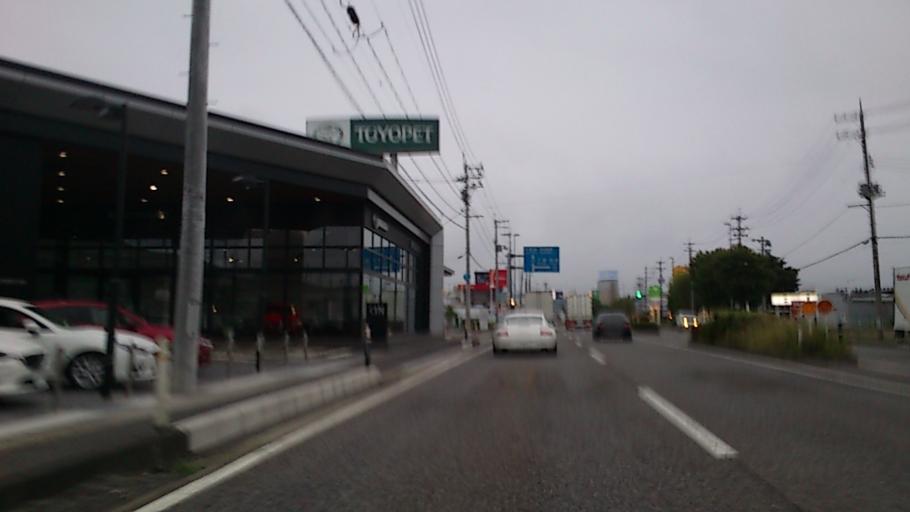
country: JP
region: Tochigi
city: Kuroiso
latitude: 37.1295
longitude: 140.1936
